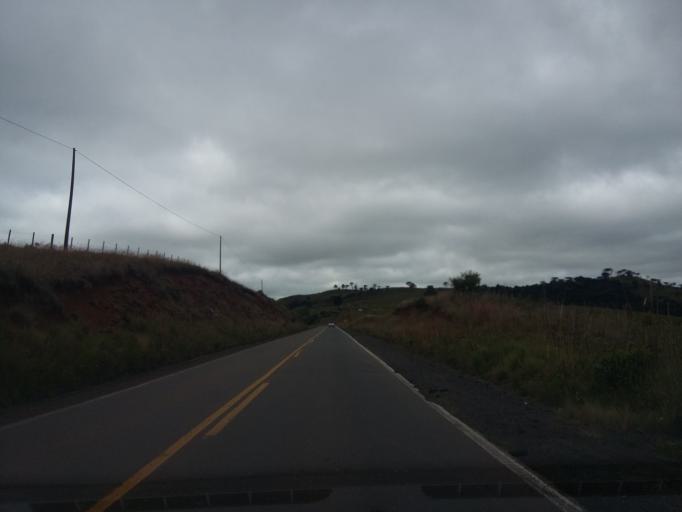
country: BR
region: Santa Catarina
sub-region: Lages
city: Lages
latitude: -27.8725
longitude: -50.1800
